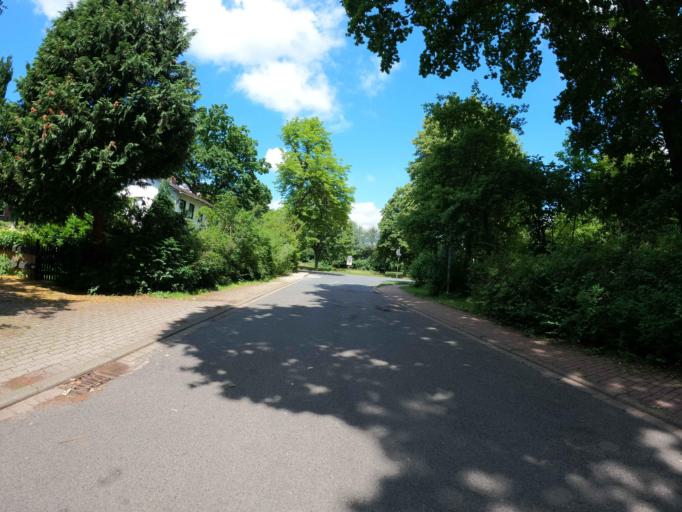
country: DE
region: Schleswig-Holstein
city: Wentorf bei Hamburg
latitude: 53.4969
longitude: 10.2564
